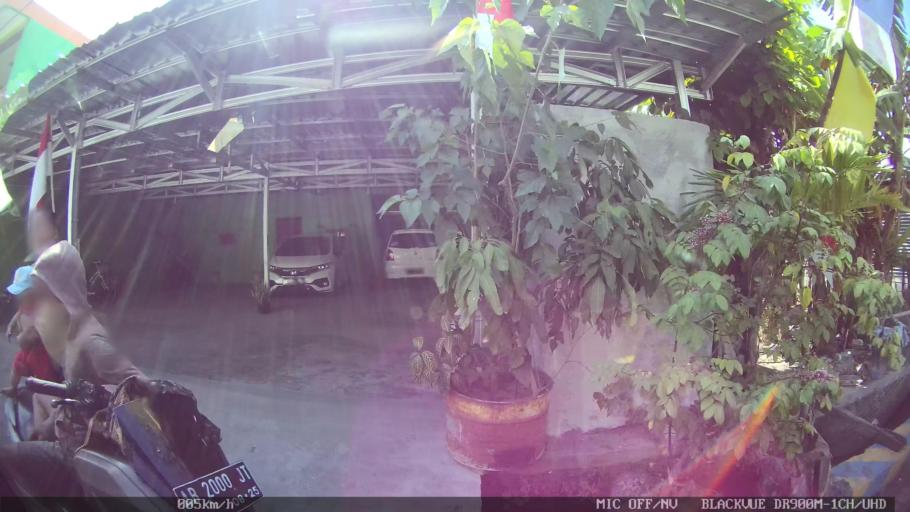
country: ID
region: Daerah Istimewa Yogyakarta
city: Kasihan
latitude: -7.8320
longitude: 110.3721
